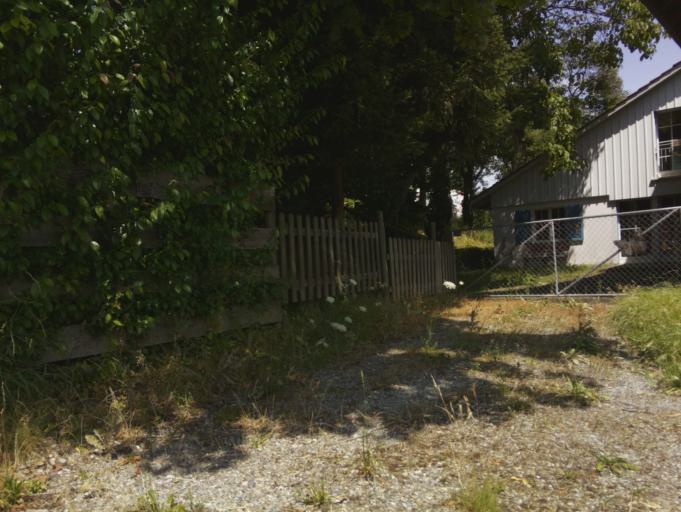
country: CH
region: Zurich
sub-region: Bezirk Andelfingen
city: Marthalen
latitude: 47.6254
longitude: 8.6740
